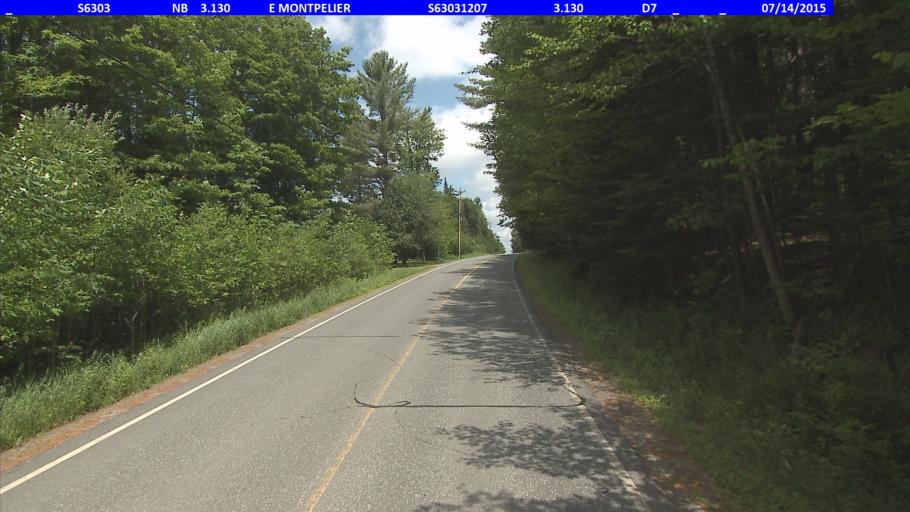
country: US
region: Vermont
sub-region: Washington County
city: Montpelier
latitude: 44.3123
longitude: -72.5282
